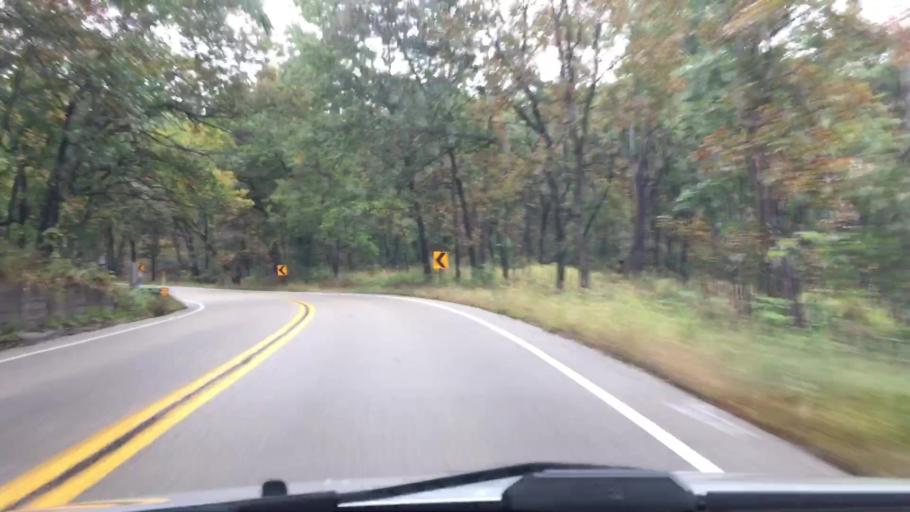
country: US
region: Wisconsin
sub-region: Waukesha County
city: Eagle
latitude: 42.9319
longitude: -88.4648
